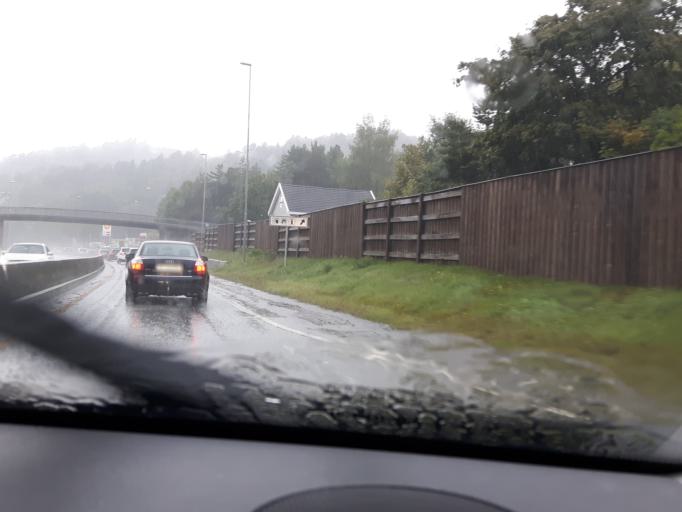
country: NO
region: Vest-Agder
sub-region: Kristiansand
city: Strai
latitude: 58.1452
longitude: 7.9168
